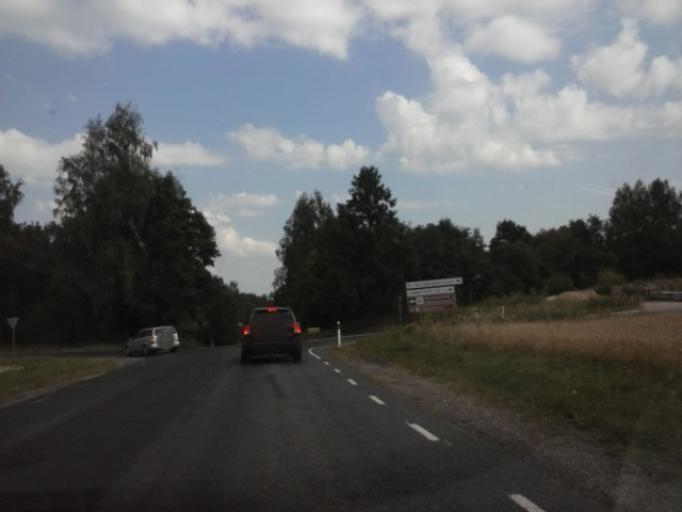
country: EE
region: Jogevamaa
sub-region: Tabivere vald
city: Tabivere
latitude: 58.5186
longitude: 26.6893
